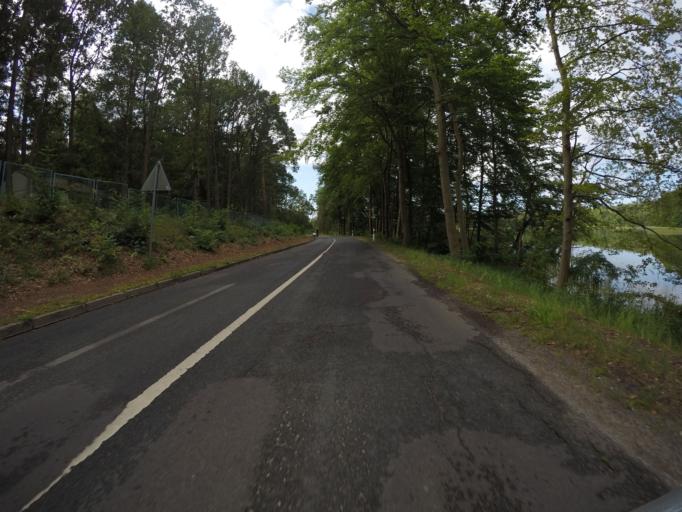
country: DE
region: Brandenburg
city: Rheinsberg
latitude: 53.1789
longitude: 12.8862
